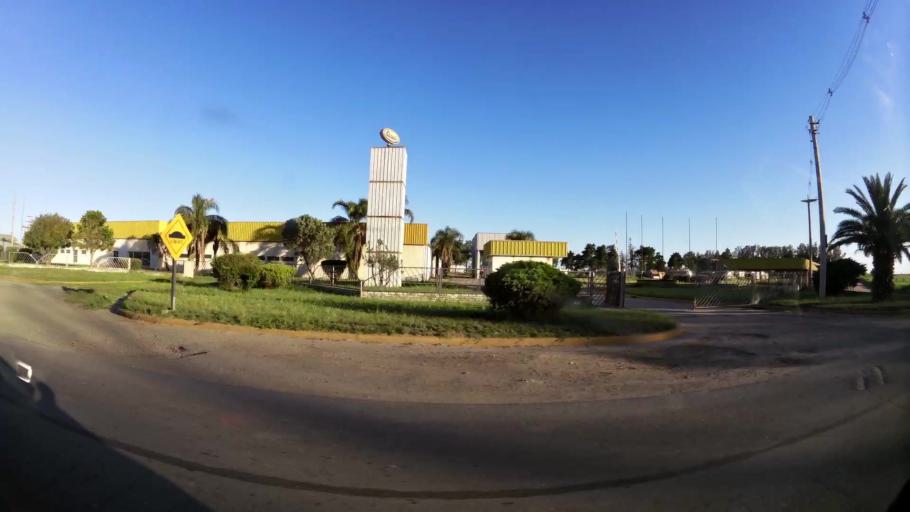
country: AR
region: Cordoba
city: Las Varillas
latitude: -31.8821
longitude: -62.7261
